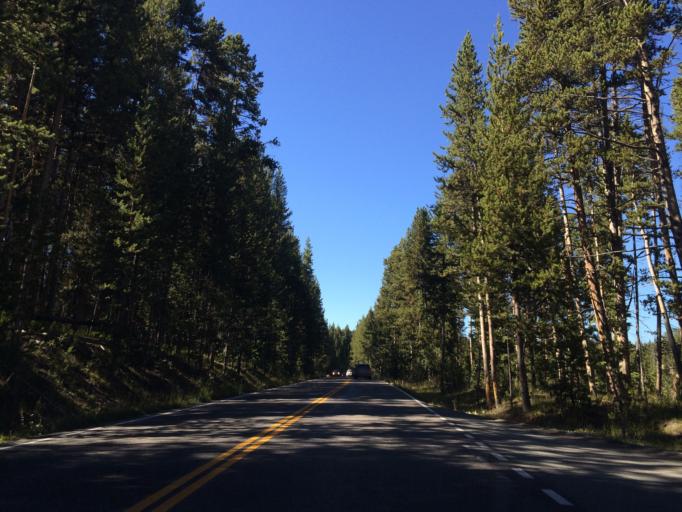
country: US
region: Montana
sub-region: Gallatin County
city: West Yellowstone
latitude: 44.6985
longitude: -110.5033
